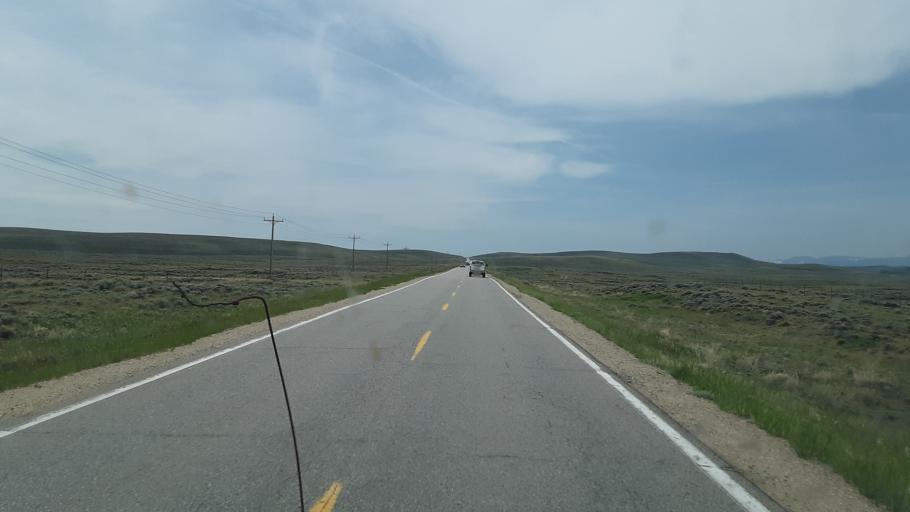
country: US
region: Colorado
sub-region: Jackson County
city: Walden
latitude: 40.6785
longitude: -106.3720
